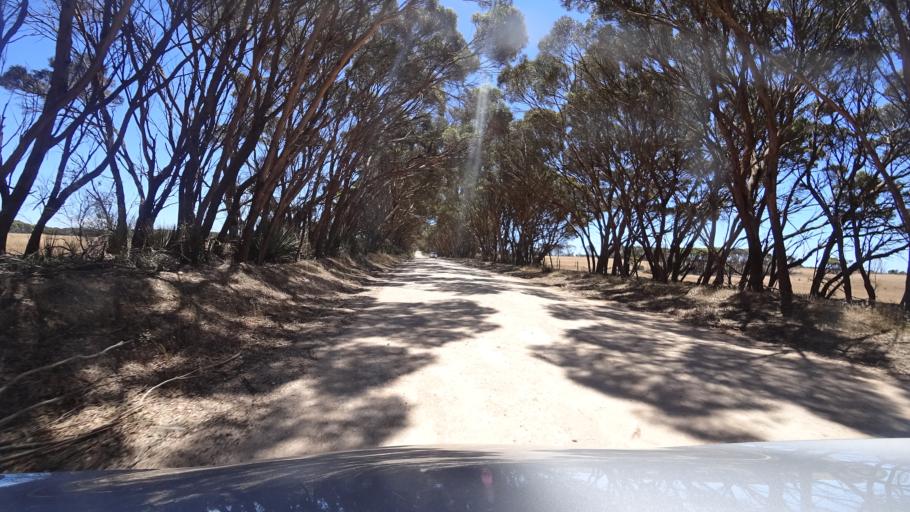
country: AU
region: South Australia
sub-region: Kangaroo Island
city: Kingscote
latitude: -35.7571
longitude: 138.0361
